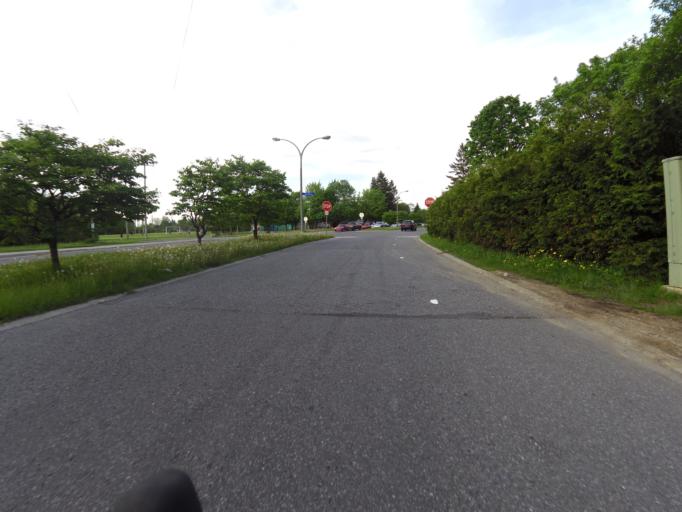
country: CA
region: Ontario
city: Bells Corners
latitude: 45.3326
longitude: -75.7761
